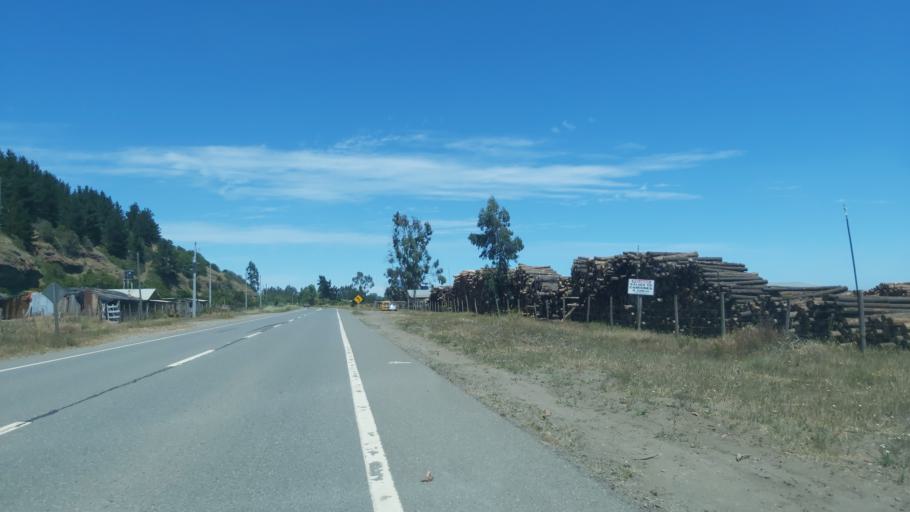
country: CL
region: Maule
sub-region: Provincia de Talca
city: Constitucion
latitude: -35.1699
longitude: -72.2661
